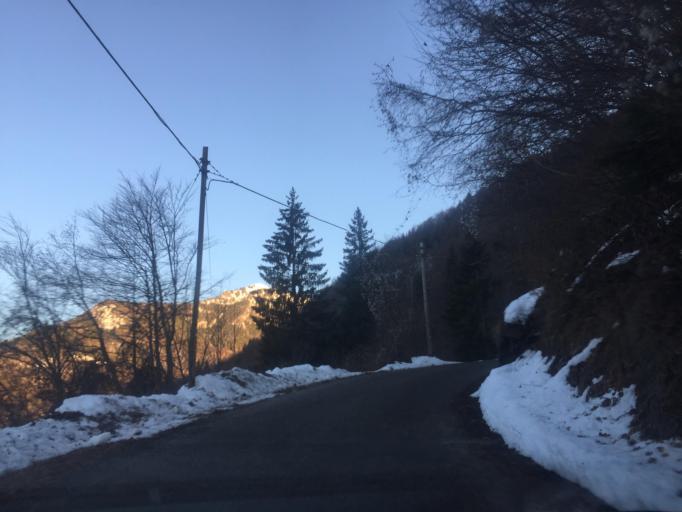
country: IT
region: Friuli Venezia Giulia
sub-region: Provincia di Udine
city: Lauco
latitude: 46.4481
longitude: 12.9316
